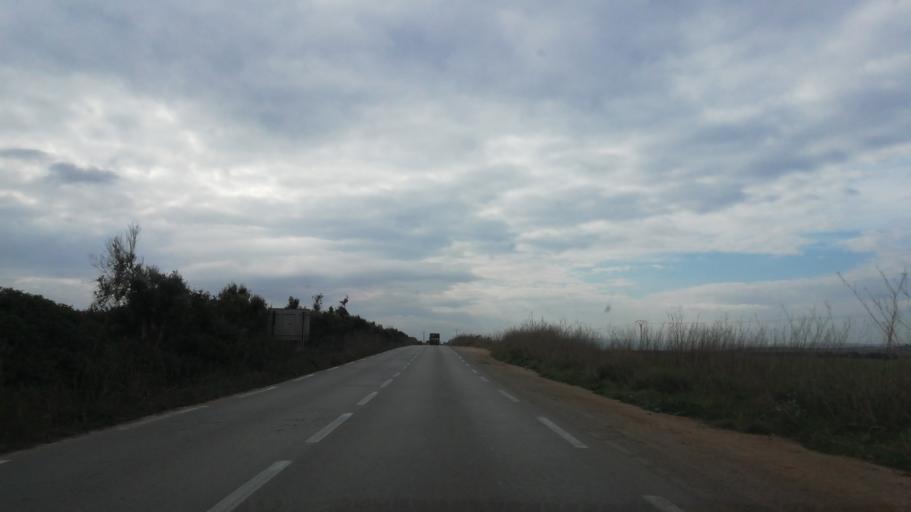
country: DZ
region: Oran
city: Ain el Bya
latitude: 35.7512
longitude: -0.3523
